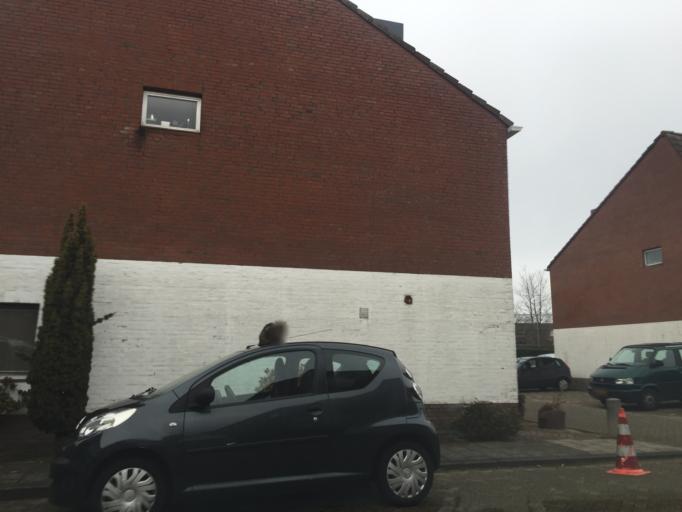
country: NL
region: South Holland
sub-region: Gemeente Leiderdorp
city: Leiderdorp
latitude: 52.1724
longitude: 4.5119
